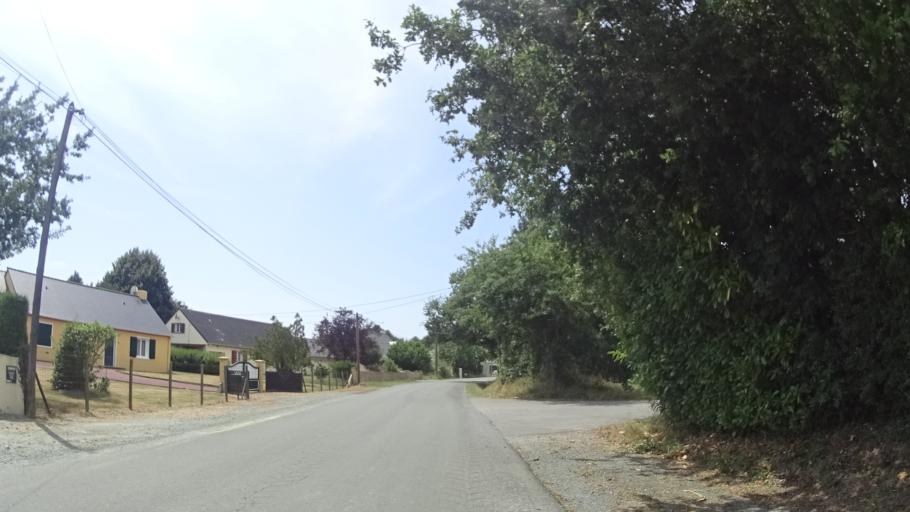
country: FR
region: Pays de la Loire
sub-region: Departement de la Loire-Atlantique
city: Fay-de-Bretagne
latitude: 47.4046
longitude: -1.7934
